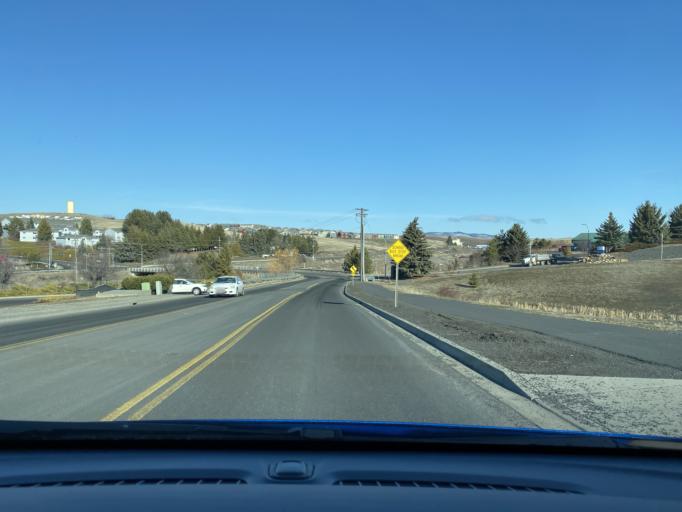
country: US
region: Washington
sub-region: Whitman County
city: Pullman
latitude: 46.7485
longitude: -117.1696
